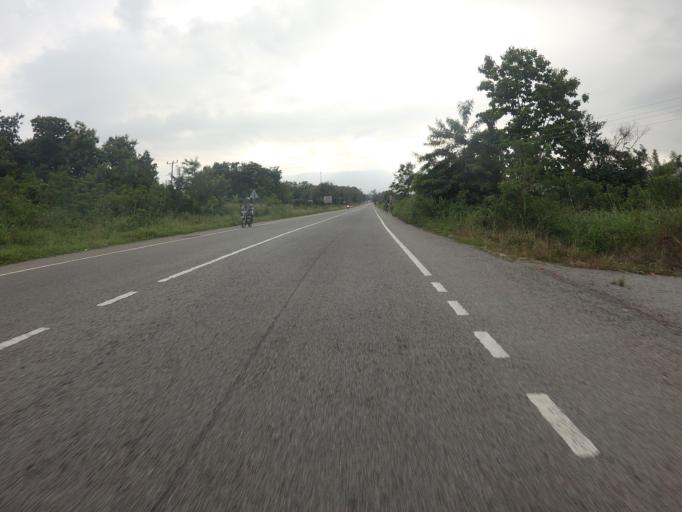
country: GH
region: Volta
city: Ho
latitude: 6.7841
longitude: 0.4475
